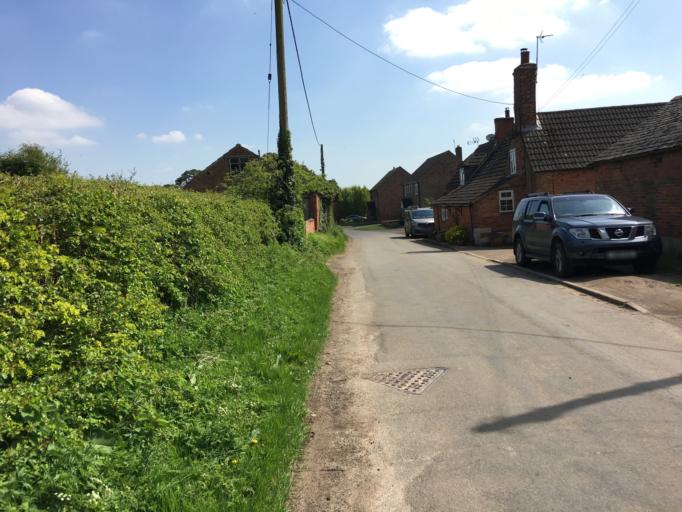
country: GB
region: England
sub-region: Leicestershire
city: Houghton on the Hill
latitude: 52.6021
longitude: -0.9761
